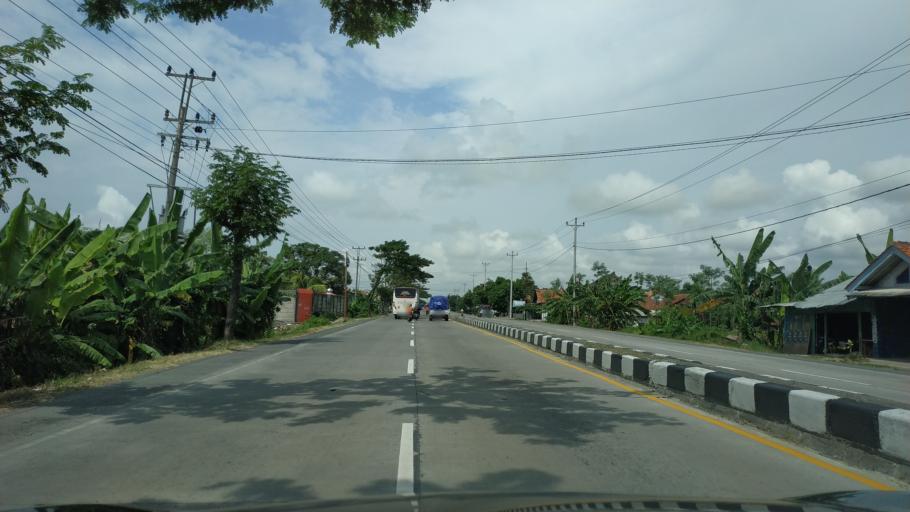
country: ID
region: Central Java
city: Tarub
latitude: -6.8704
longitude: 109.2344
